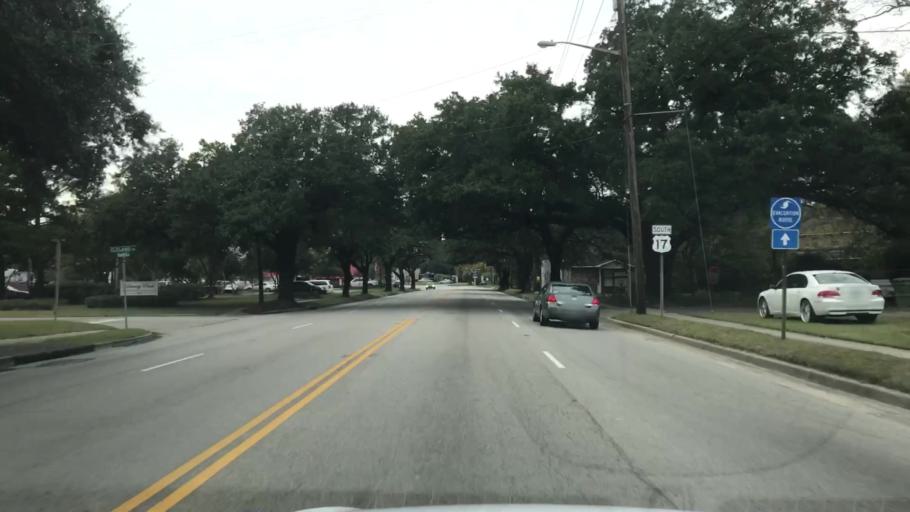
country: US
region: South Carolina
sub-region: Georgetown County
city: Georgetown
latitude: 33.3742
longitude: -79.2838
